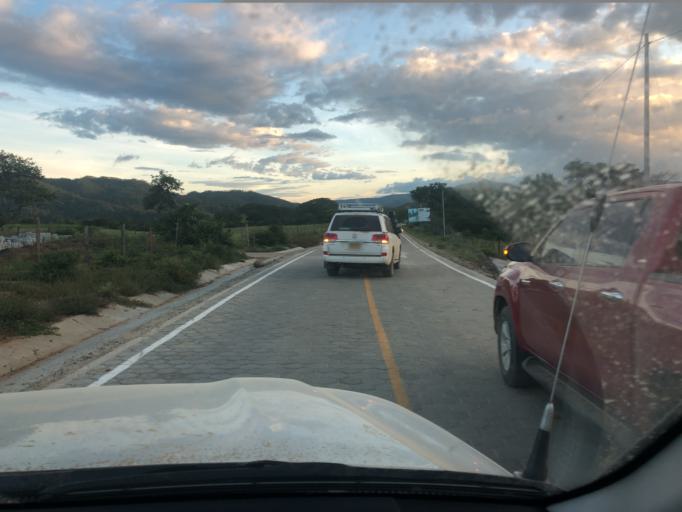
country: HN
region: El Paraiso
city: Santa Cruz
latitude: 13.7274
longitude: -86.6224
